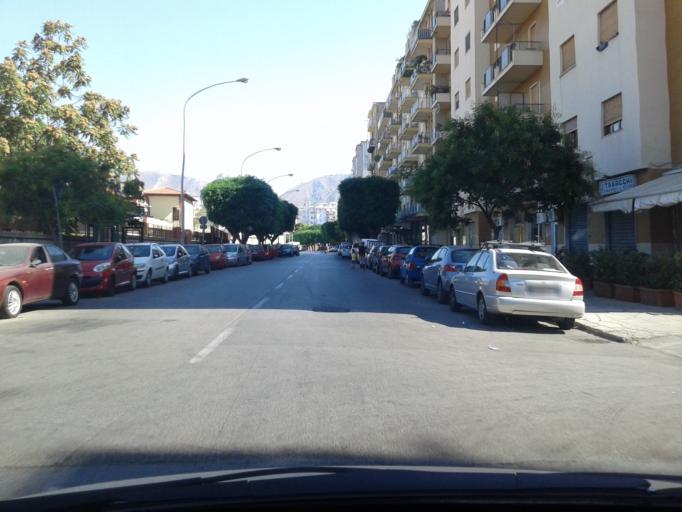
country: IT
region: Sicily
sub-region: Palermo
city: Palermo
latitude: 38.1038
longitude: 13.3357
